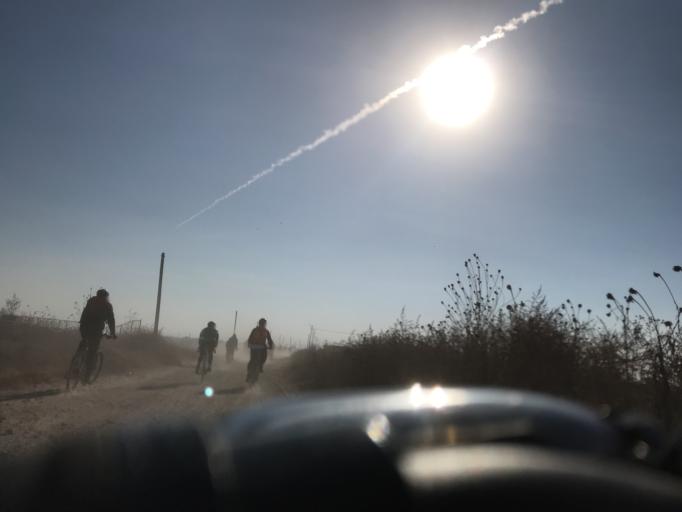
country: MX
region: Mexico
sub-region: Nextlalpan
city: Ex-Hacienda Santa Ines
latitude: 19.6973
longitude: -99.0747
